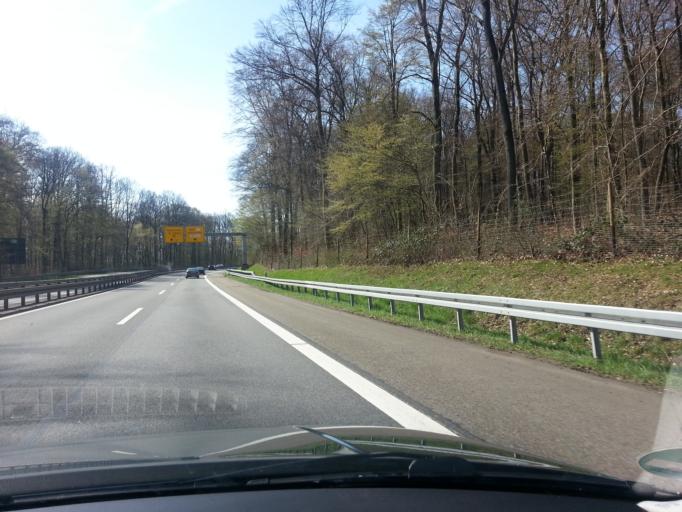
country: DE
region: Saarland
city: Saarbrucken
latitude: 49.2630
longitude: 6.9939
